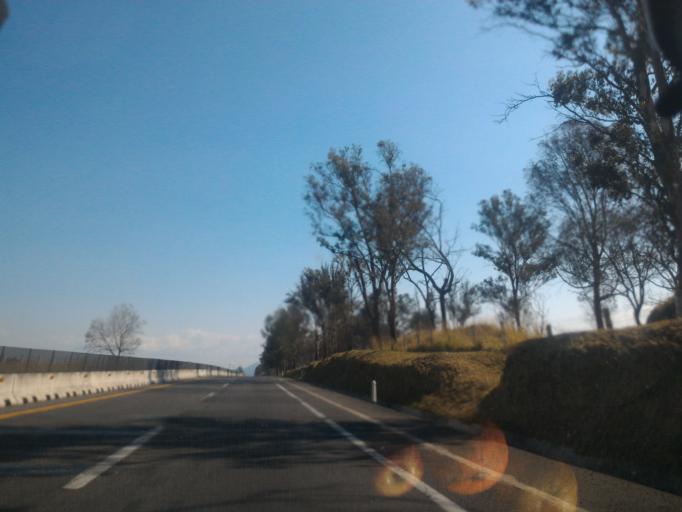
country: MX
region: Jalisco
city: Zapotiltic
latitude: 19.6155
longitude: -103.4604
